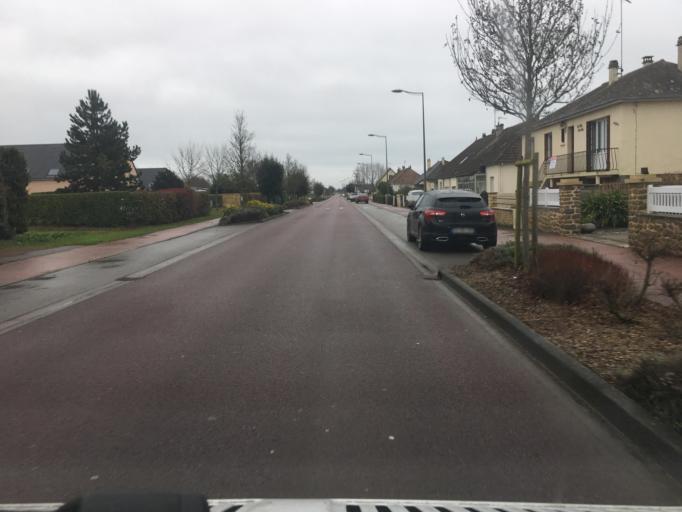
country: FR
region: Lower Normandy
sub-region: Departement de la Manche
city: Quettehou
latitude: 49.5909
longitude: -1.2925
